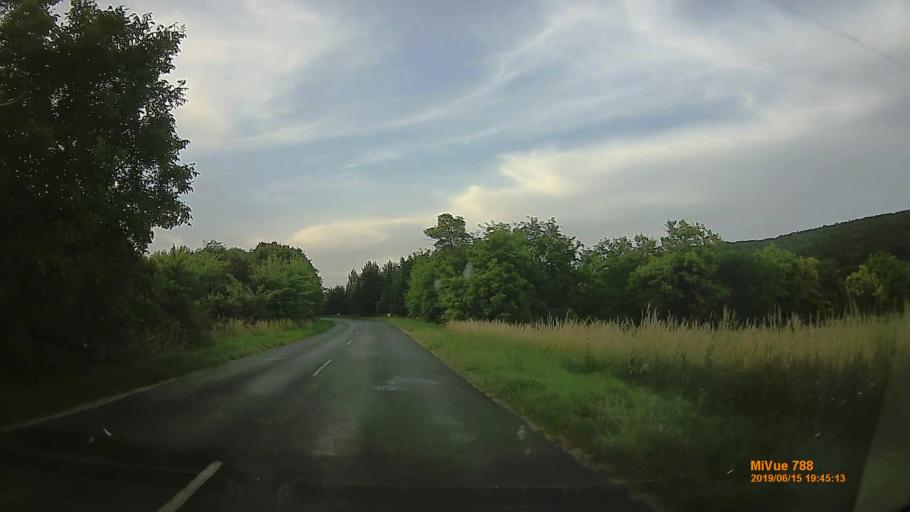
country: HU
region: Veszprem
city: Szentkiralyszabadja
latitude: 47.0073
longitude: 17.9654
